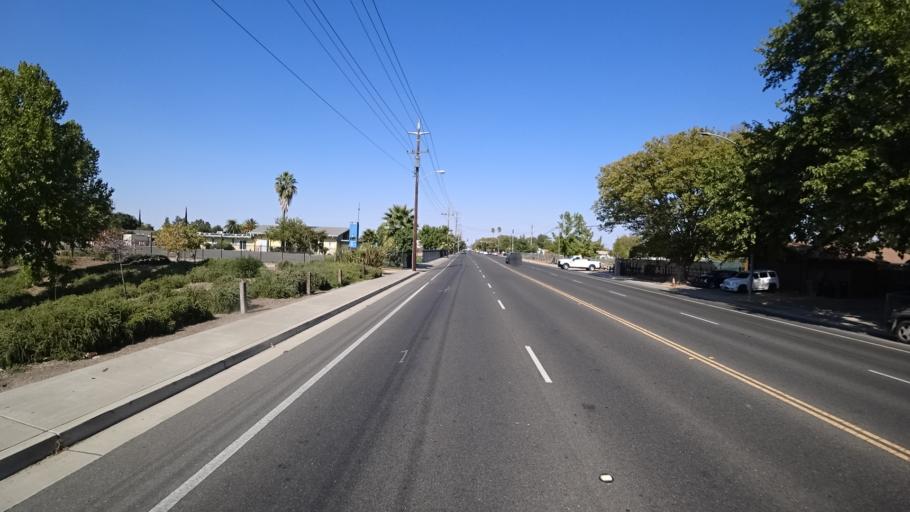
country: US
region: California
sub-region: Sacramento County
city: Parkway
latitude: 38.4853
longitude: -121.4804
